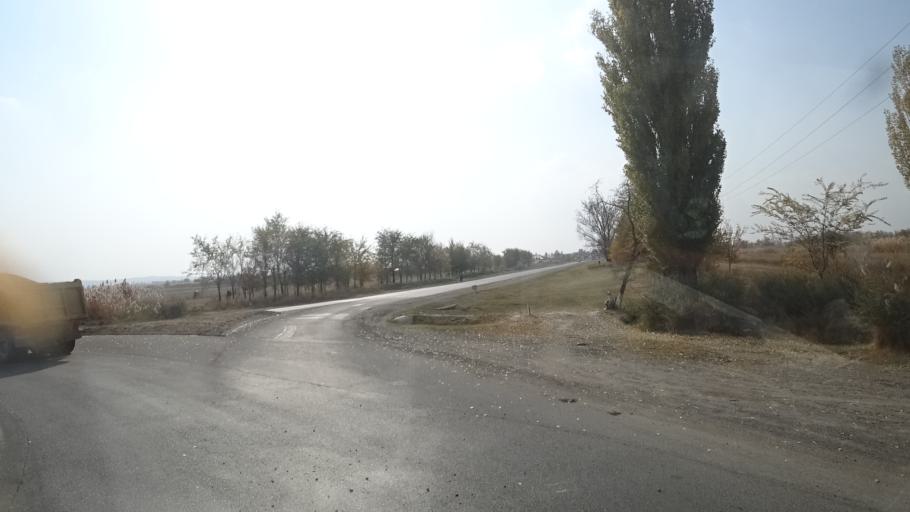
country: KZ
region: Zhambyl
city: Sarykemer
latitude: 42.9372
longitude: 71.4432
